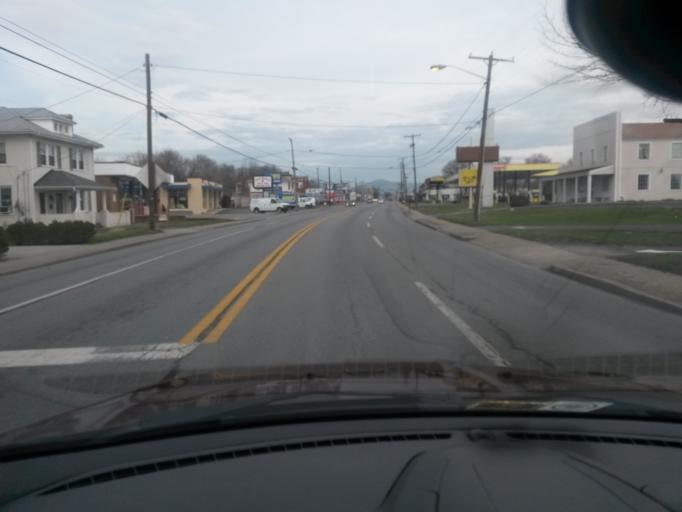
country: US
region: Virginia
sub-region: City of Roanoke
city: Roanoke
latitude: 37.3021
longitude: -79.9435
